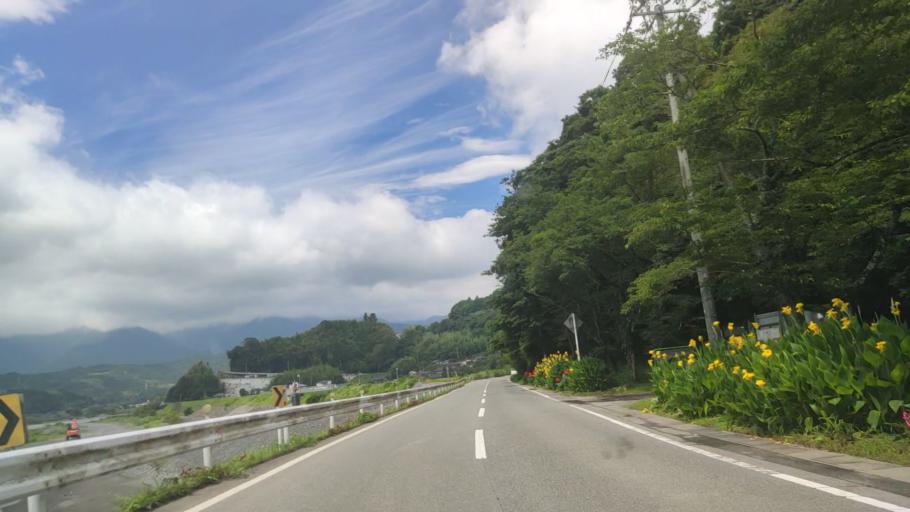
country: JP
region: Shizuoka
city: Fujinomiya
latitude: 35.2412
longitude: 138.5042
